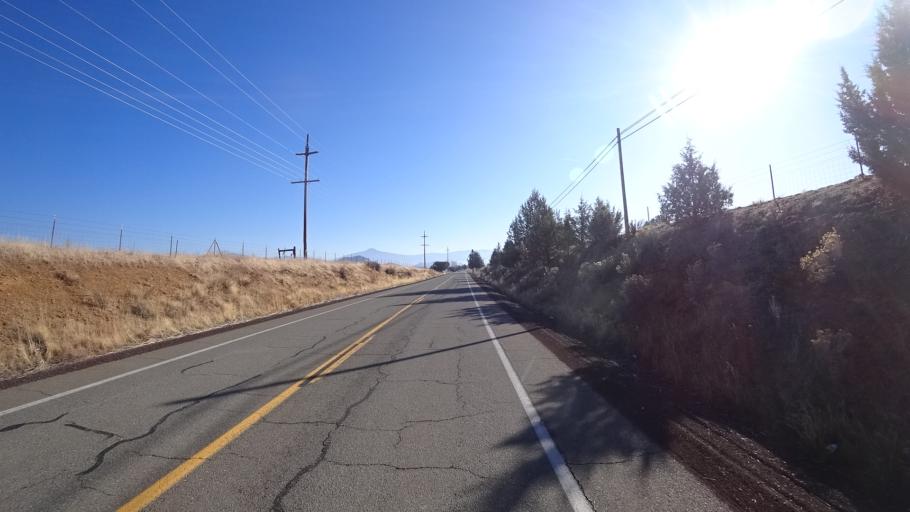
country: US
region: California
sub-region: Siskiyou County
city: Montague
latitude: 41.7108
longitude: -122.5811
